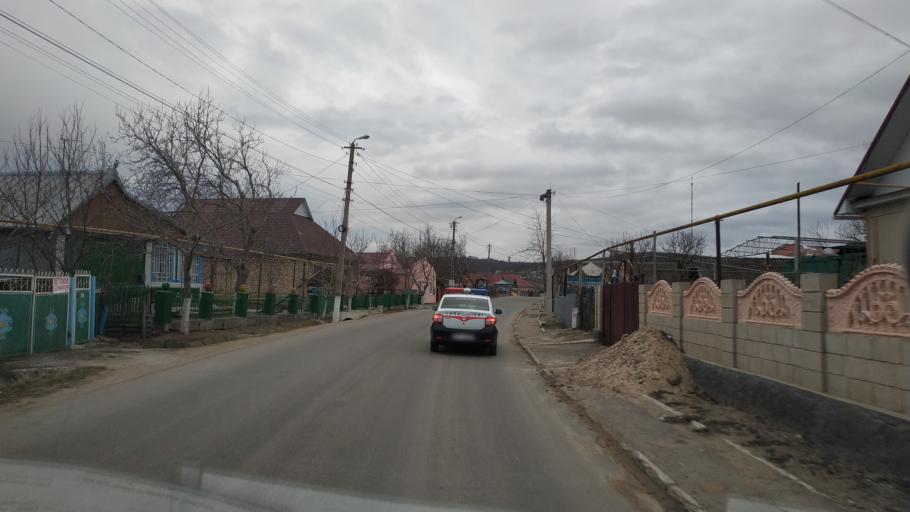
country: MD
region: Causeni
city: Causeni
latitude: 46.6529
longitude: 29.4438
